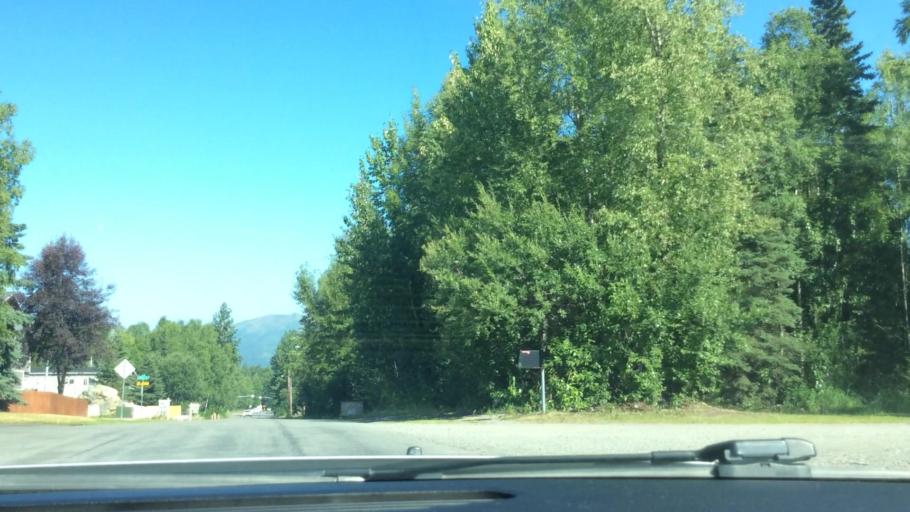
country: US
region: Alaska
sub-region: Anchorage Municipality
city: Anchorage
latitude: 61.1989
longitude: -149.7851
